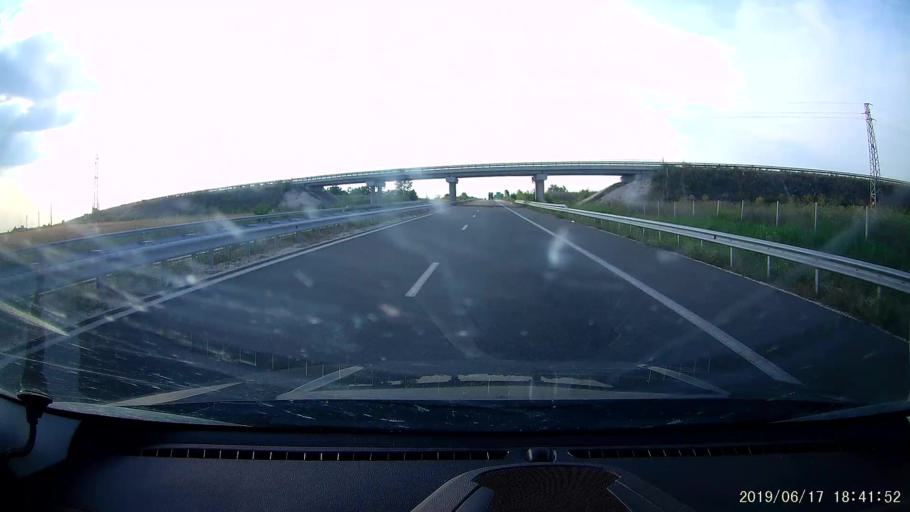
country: BG
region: Stara Zagora
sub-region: Obshtina Chirpan
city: Chirpan
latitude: 42.1805
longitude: 25.2476
